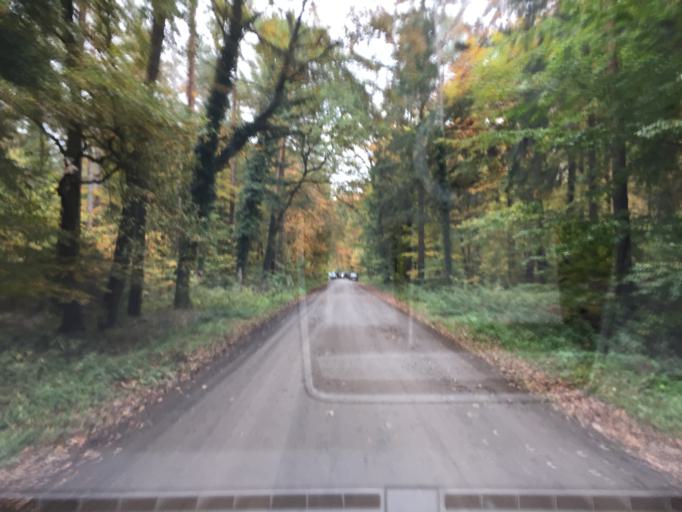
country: DE
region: Lower Saxony
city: Linsburg
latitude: 52.5740
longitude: 9.3126
